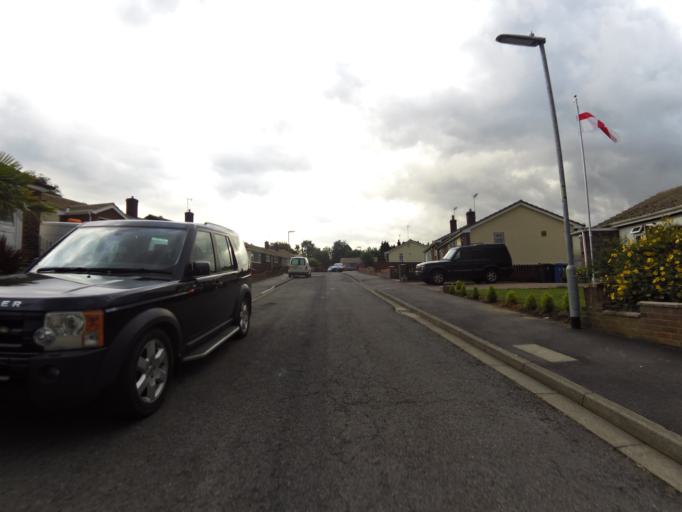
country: GB
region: England
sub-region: Suffolk
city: Ipswich
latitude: 52.0745
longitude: 1.1446
